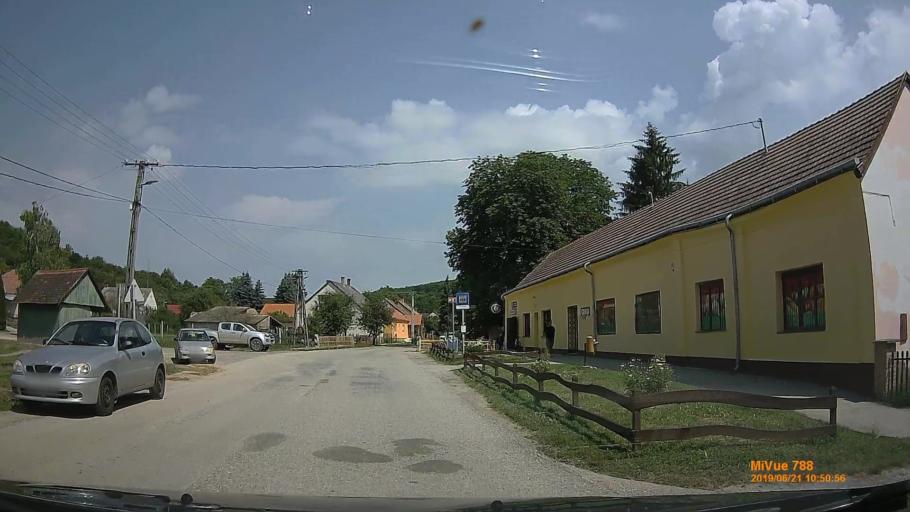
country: HU
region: Baranya
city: Buekkoesd
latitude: 46.1328
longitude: 18.0440
